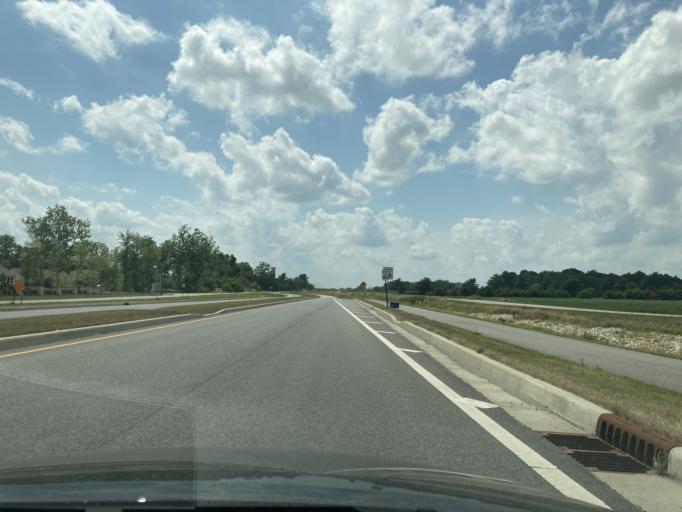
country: US
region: Indiana
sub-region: Boone County
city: Zionsville
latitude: 39.9994
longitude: -86.2032
